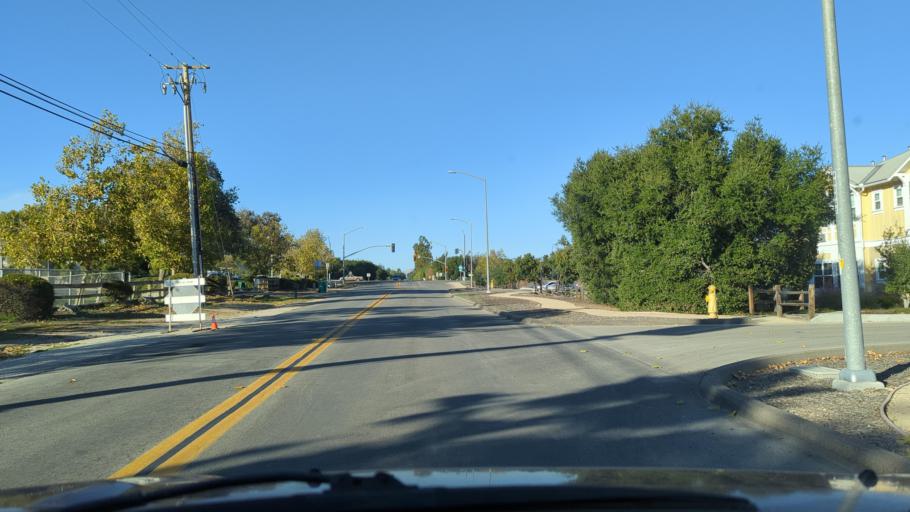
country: US
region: California
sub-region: Santa Barbara County
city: Santa Ynez
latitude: 34.6052
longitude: -120.0981
